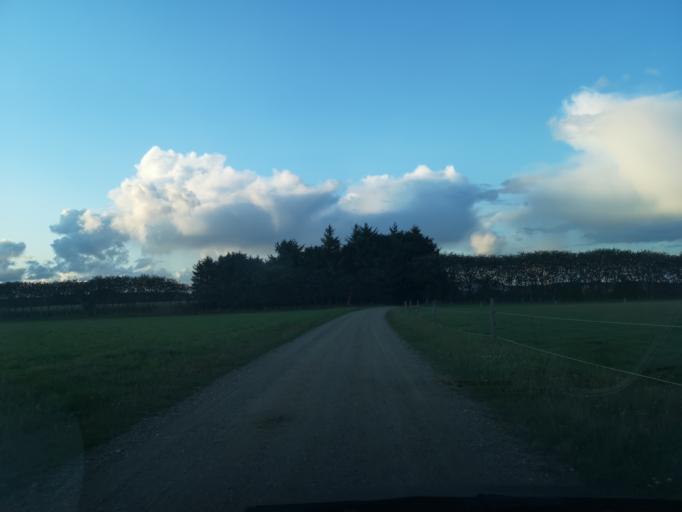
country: DK
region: Central Jutland
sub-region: Ringkobing-Skjern Kommune
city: Videbaek
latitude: 56.0569
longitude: 8.5886
